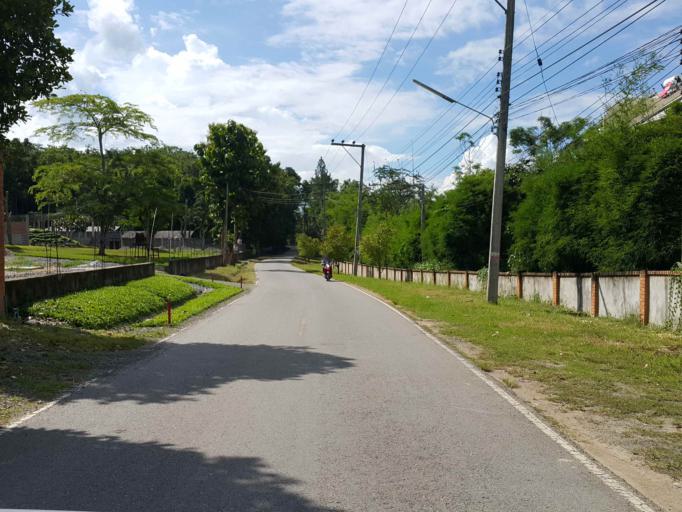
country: TH
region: Chiang Mai
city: Mae Taeng
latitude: 18.9651
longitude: 98.9120
